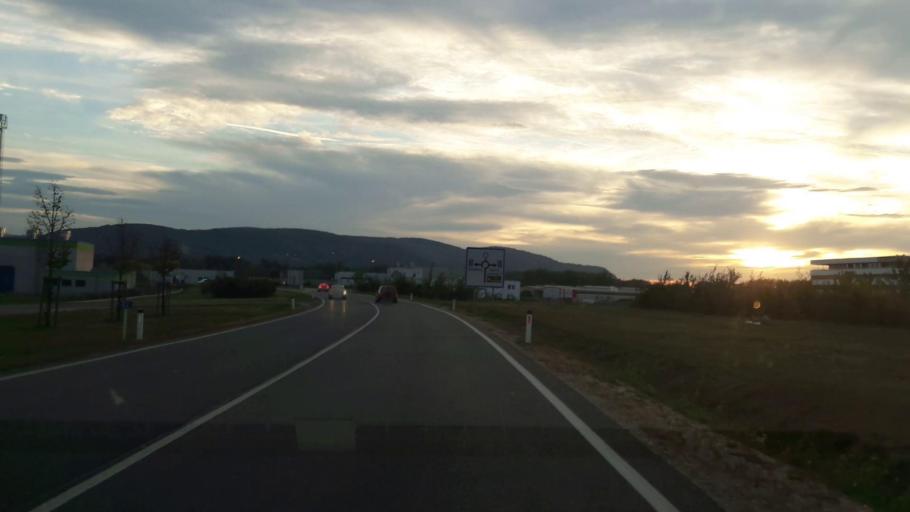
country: AT
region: Lower Austria
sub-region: Politischer Bezirk Korneuburg
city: Leobendorf
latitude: 48.3630
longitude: 16.3122
